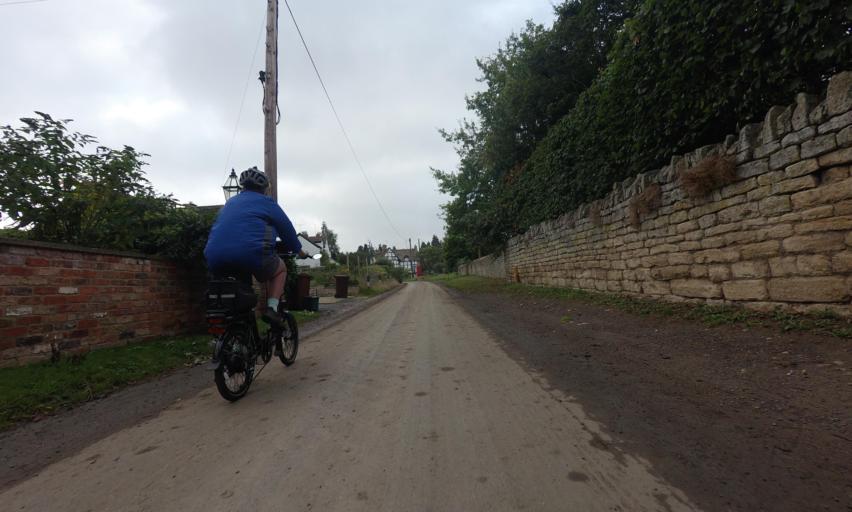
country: GB
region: England
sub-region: Gloucestershire
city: Gotherington
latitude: 51.9908
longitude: -2.0263
